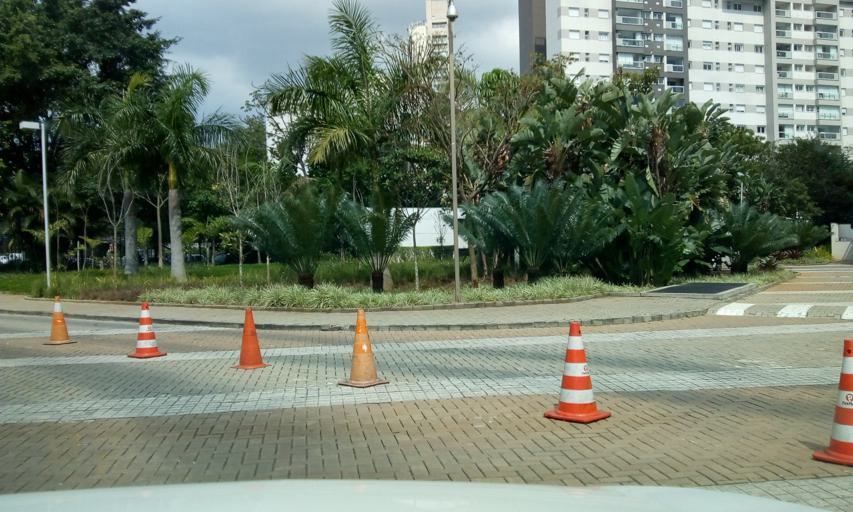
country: BR
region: Sao Paulo
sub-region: Sao Paulo
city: Sao Paulo
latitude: -23.5983
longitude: -46.6895
